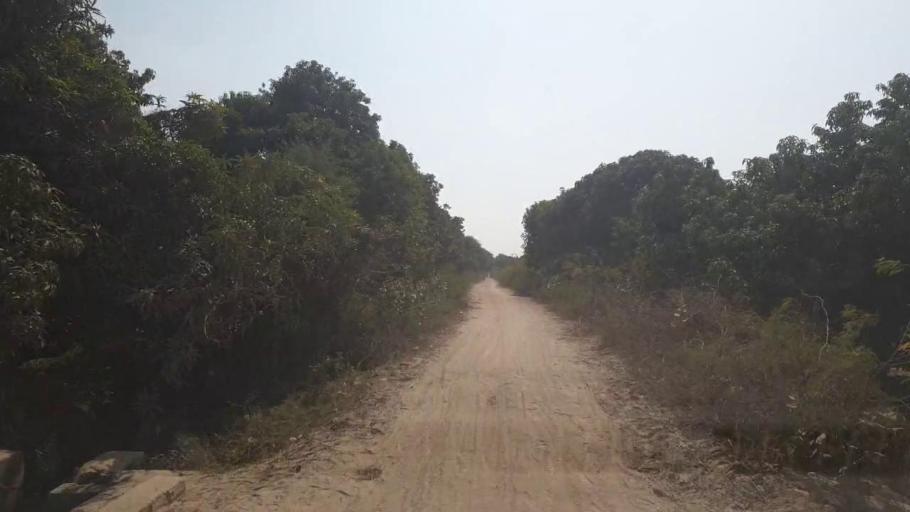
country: PK
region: Sindh
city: Tando Allahyar
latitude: 25.4757
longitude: 68.8500
